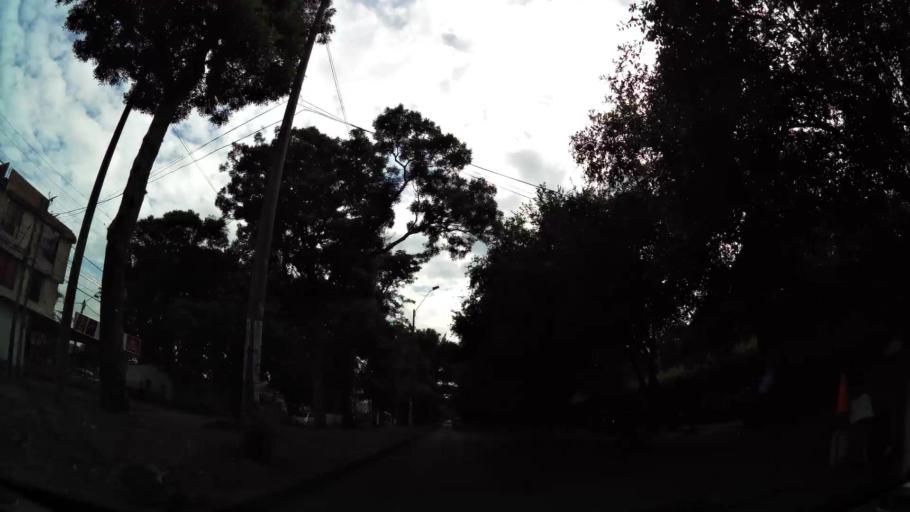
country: CO
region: Valle del Cauca
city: Cali
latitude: 3.4686
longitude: -76.5004
